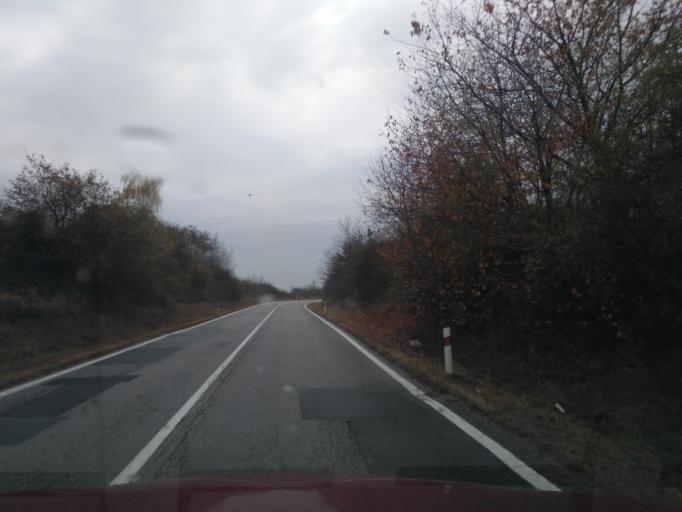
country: SK
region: Kosicky
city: Kosice
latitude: 48.6810
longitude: 21.1869
